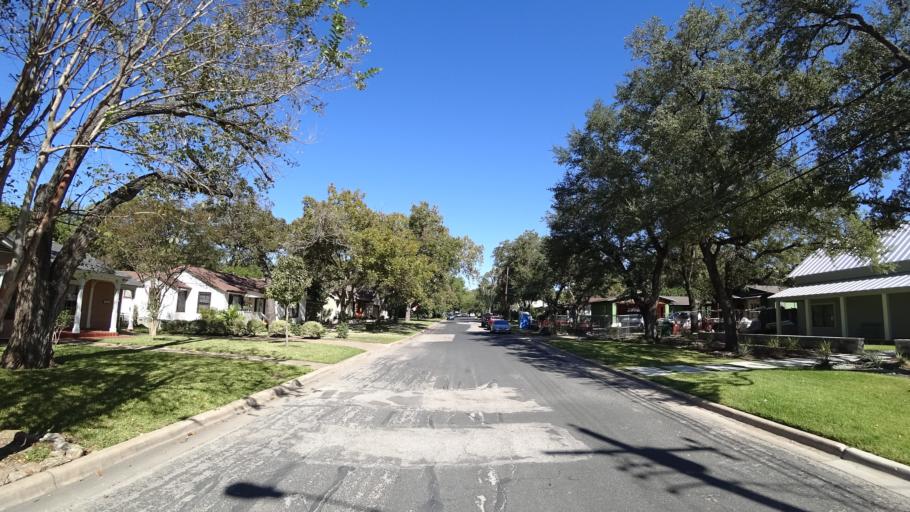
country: US
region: Texas
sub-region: Travis County
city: Austin
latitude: 30.3310
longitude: -97.7444
